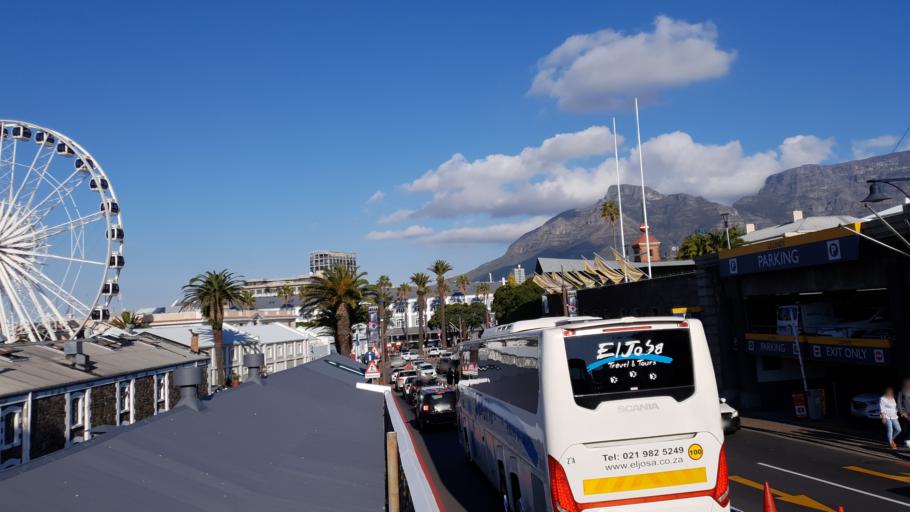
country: ZA
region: Western Cape
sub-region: City of Cape Town
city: Cape Town
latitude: -33.9048
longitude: 18.4188
